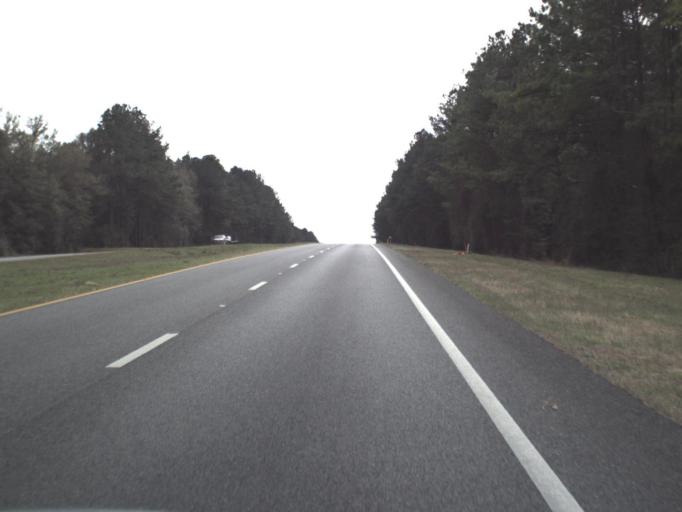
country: US
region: Florida
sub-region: Bay County
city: Youngstown
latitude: 30.5568
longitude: -85.3898
